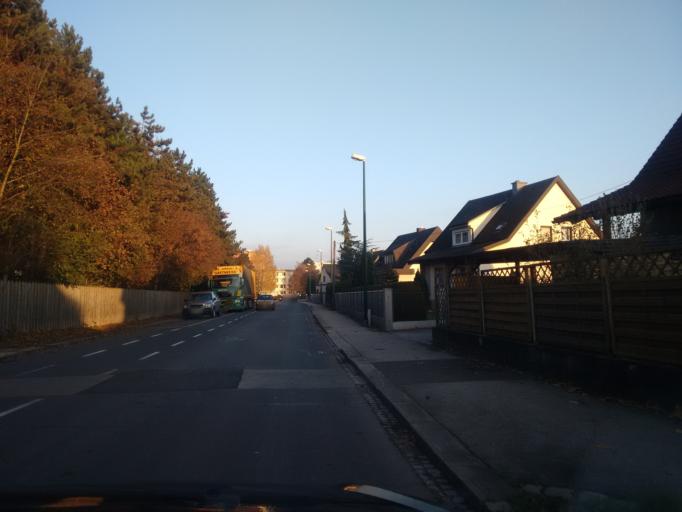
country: AT
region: Upper Austria
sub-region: Wels-Land
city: Thalheim bei Wels
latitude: 48.1572
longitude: 13.9916
